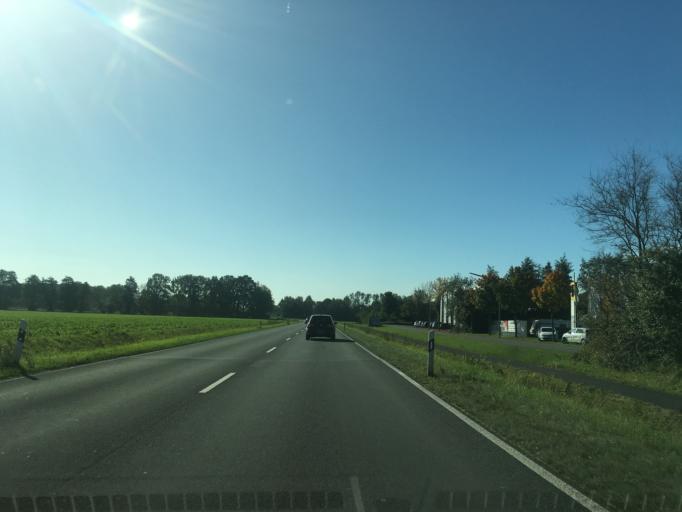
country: DE
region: North Rhine-Westphalia
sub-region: Regierungsbezirk Munster
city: Senden
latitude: 51.8445
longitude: 7.4883
